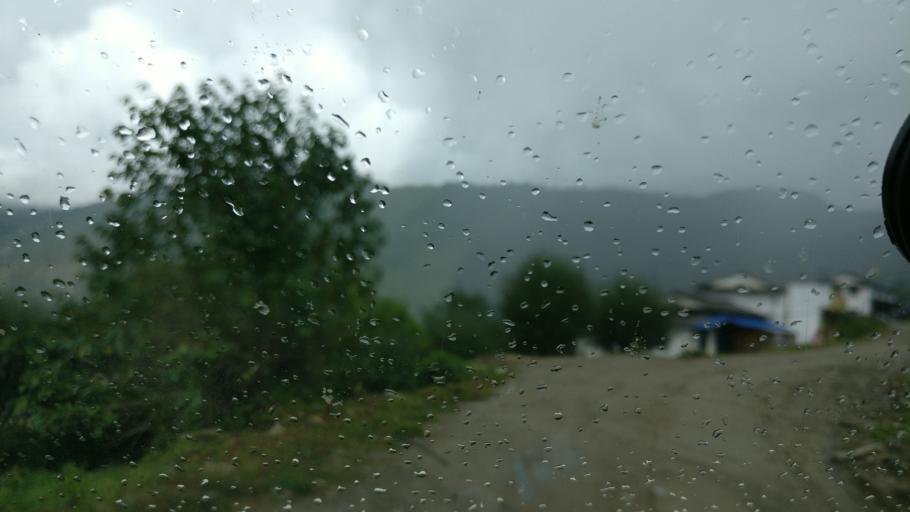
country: NP
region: Western Region
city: Baglung
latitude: 28.2836
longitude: 83.6433
